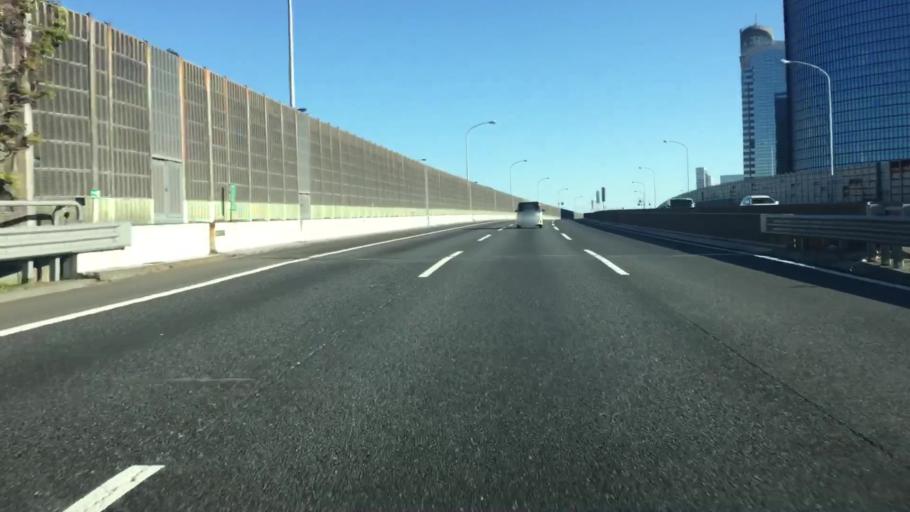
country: JP
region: Chiba
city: Funabashi
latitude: 35.6580
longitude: 140.0368
